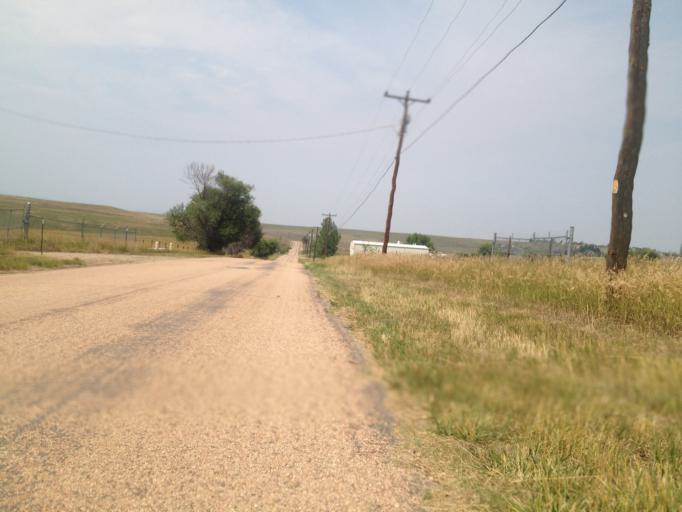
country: US
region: Colorado
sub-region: Boulder County
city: Superior
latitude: 39.9516
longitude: -105.1989
